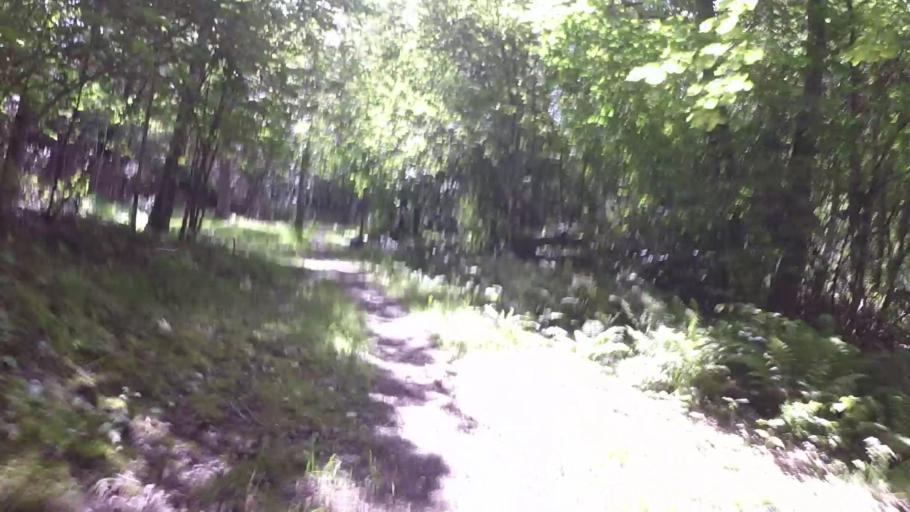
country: SE
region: Vaestra Goetaland
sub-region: Trollhattan
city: Trollhattan
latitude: 58.2531
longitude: 12.2672
